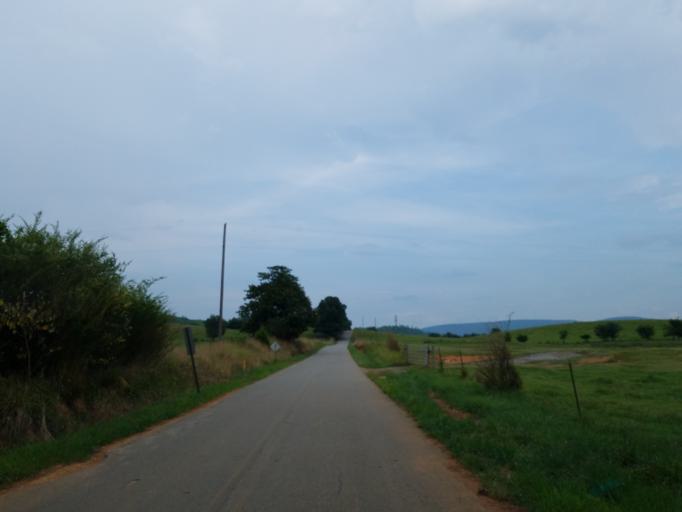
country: US
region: Georgia
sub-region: Bartow County
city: Rydal
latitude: 34.3720
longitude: -84.7018
